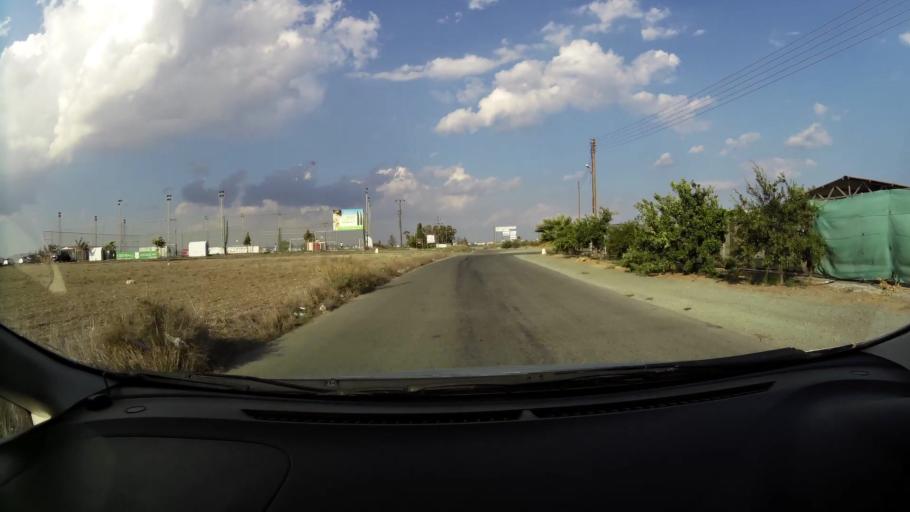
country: CY
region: Larnaka
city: Dhromolaxia
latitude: 34.8843
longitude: 33.5934
